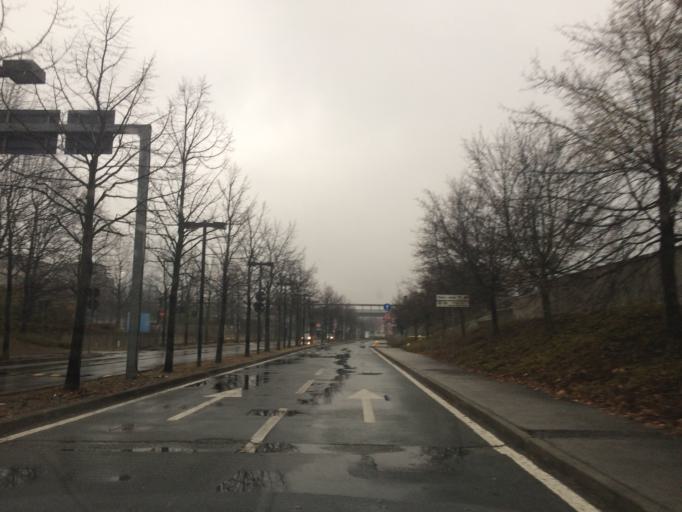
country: IT
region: Piedmont
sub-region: Provincia di Torino
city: Moncalieri
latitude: 45.0332
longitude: 7.6638
